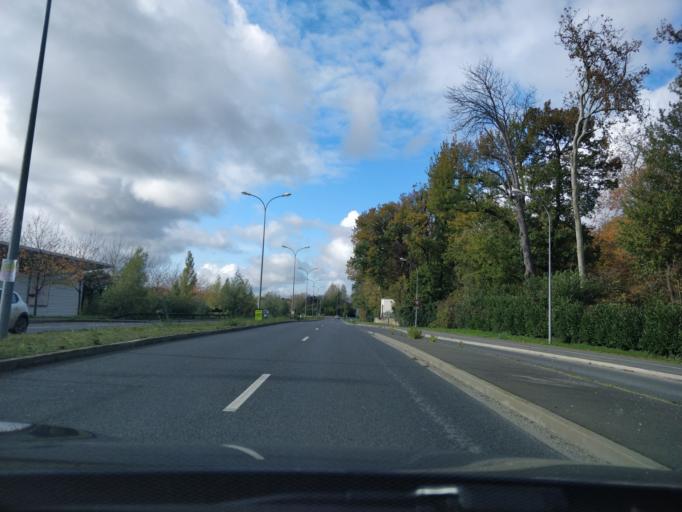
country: FR
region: Ile-de-France
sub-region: Departement de l'Essonne
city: Arpajon
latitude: 48.5998
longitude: 2.2386
